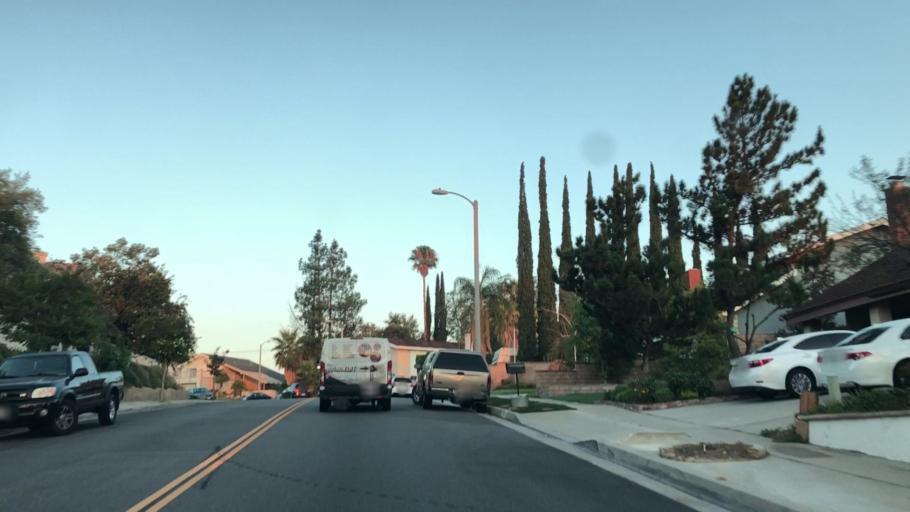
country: US
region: California
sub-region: Los Angeles County
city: Santa Clarita
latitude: 34.3958
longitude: -118.4742
